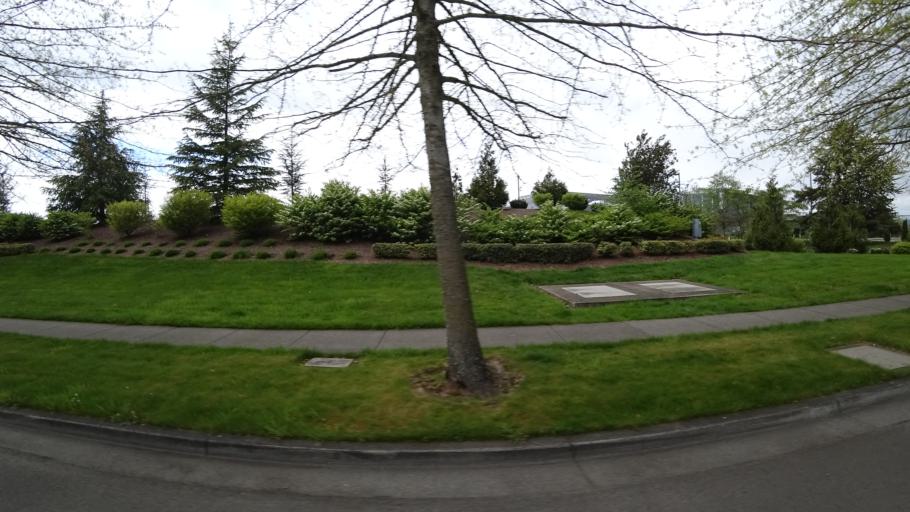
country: US
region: Oregon
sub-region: Washington County
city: Rockcreek
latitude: 45.5381
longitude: -122.9201
